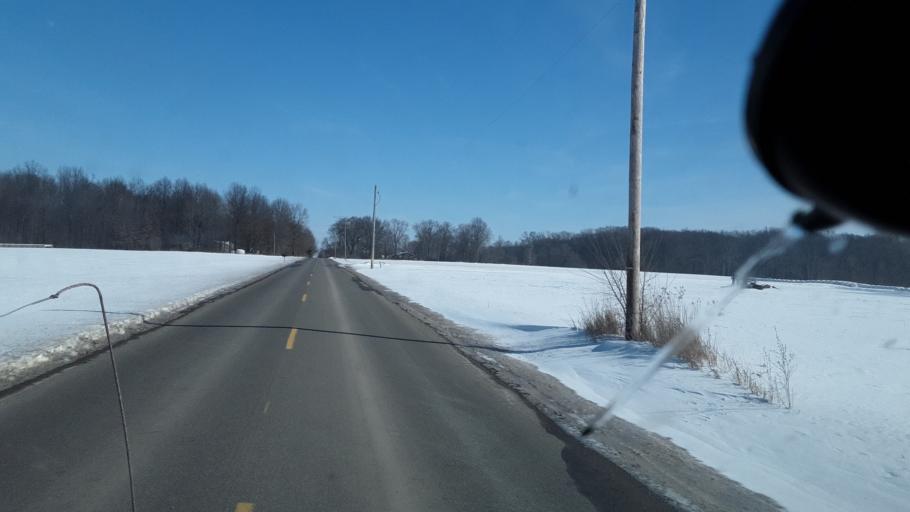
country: US
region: Ohio
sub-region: Mahoning County
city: Sebring
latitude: 40.9594
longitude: -81.0456
